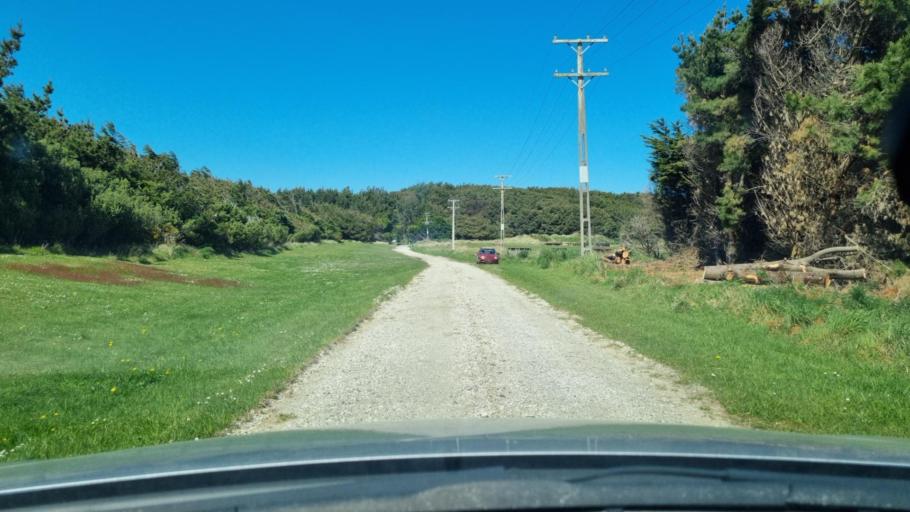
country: NZ
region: Southland
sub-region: Invercargill City
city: Invercargill
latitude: -46.4392
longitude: 168.2393
